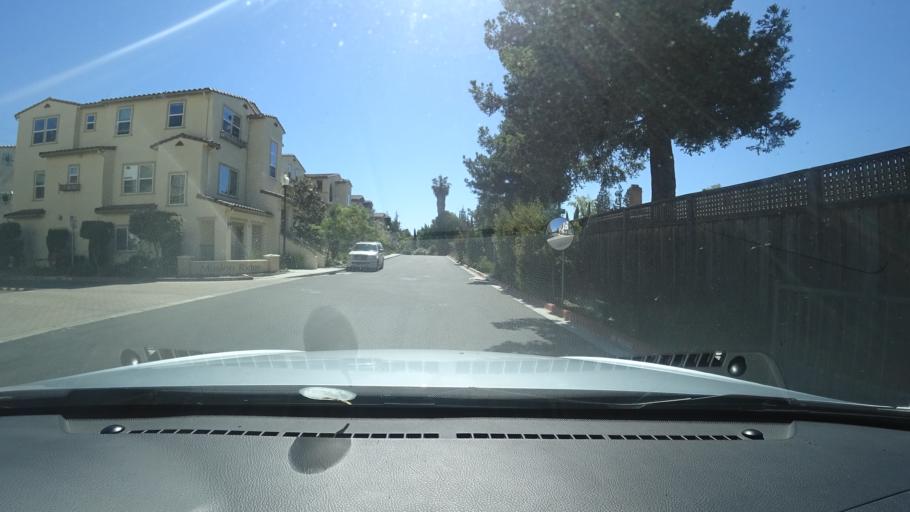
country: US
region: California
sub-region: Alameda County
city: Fremont
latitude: 37.5249
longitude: -121.9196
